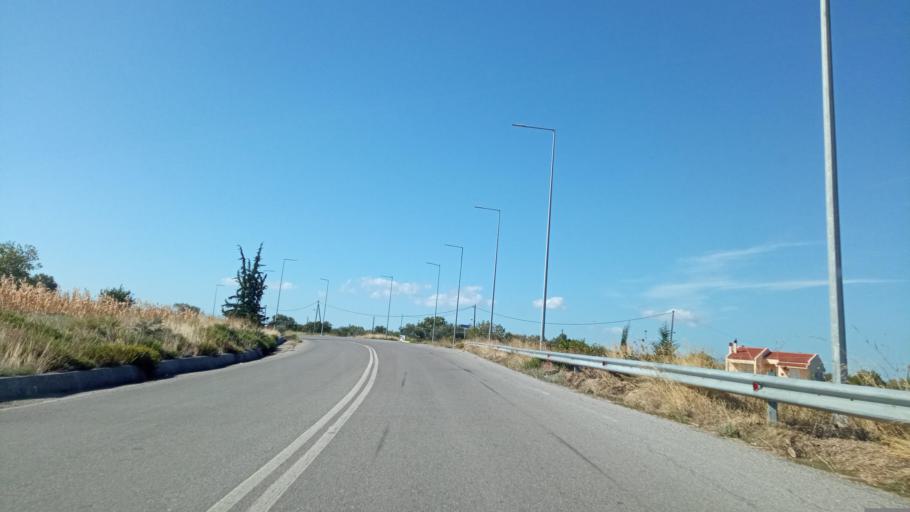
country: GR
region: Central Greece
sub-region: Nomos Evvoias
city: Psachna
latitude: 38.5834
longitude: 23.7699
